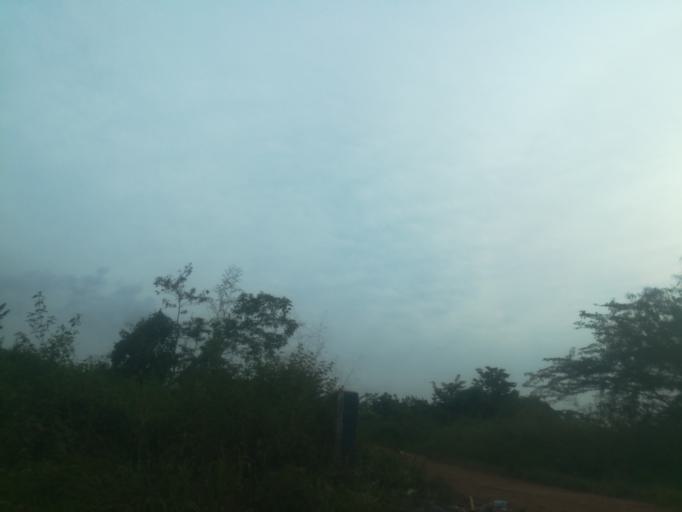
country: NG
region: Ogun
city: Ayetoro
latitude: 7.2133
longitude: 3.1847
